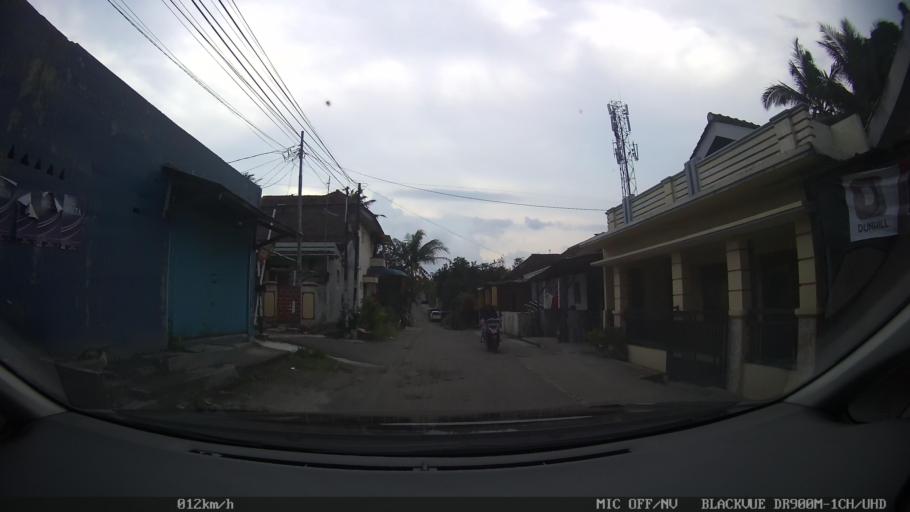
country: ID
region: Lampung
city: Kedaton
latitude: -5.3944
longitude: 105.2049
